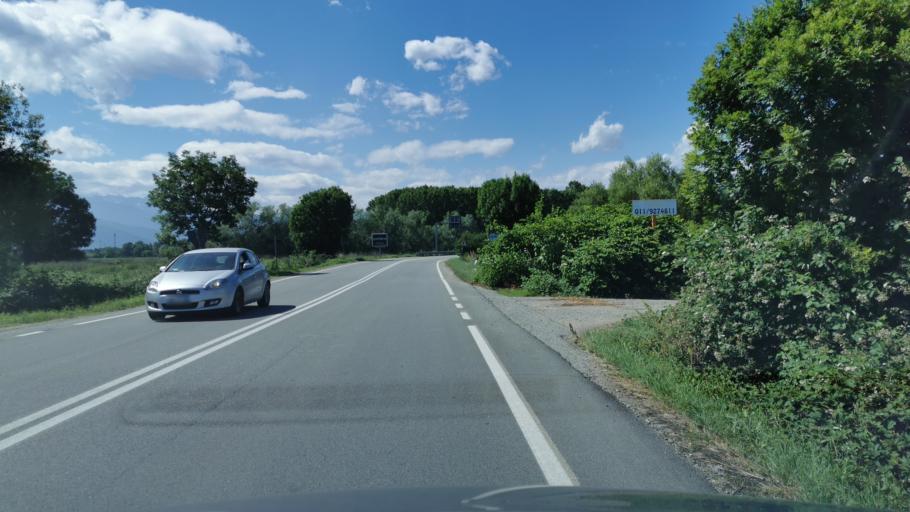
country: IT
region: Piedmont
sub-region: Provincia di Torino
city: Airasca
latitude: 44.9198
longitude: 7.4949
